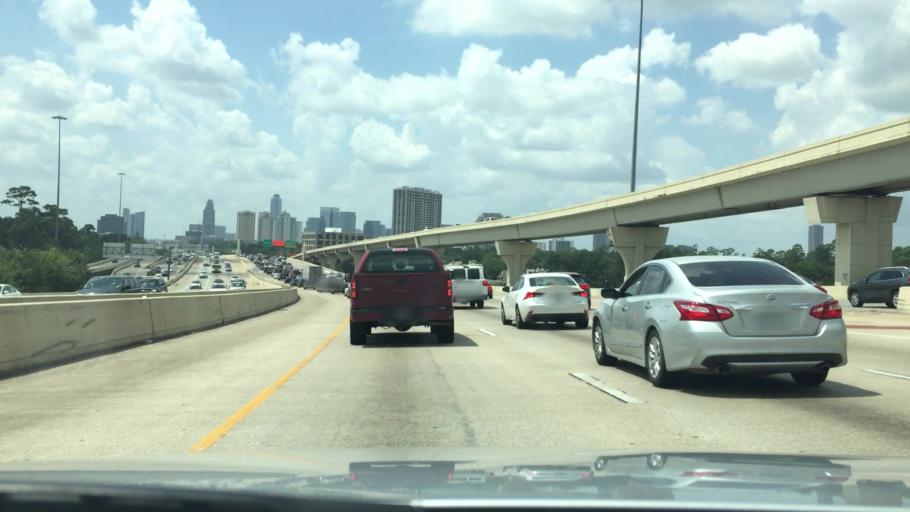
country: US
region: Texas
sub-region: Harris County
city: Hunters Creek Village
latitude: 29.7769
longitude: -95.4541
